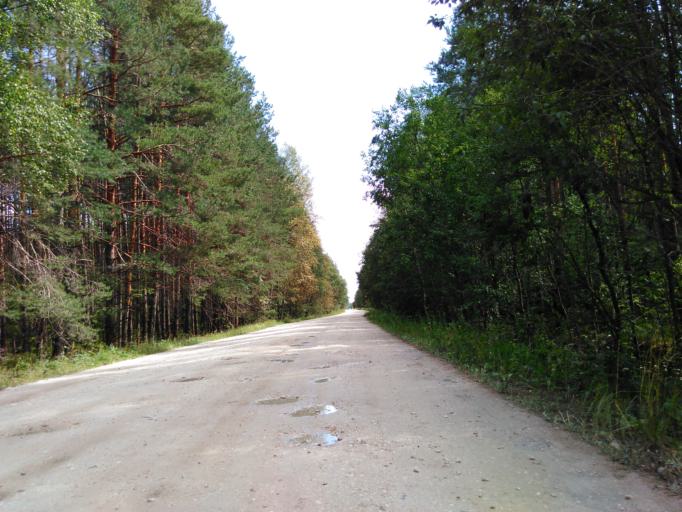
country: RU
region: Vladimir
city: Krasnyy Oktyabr'
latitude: 56.0054
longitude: 38.8353
